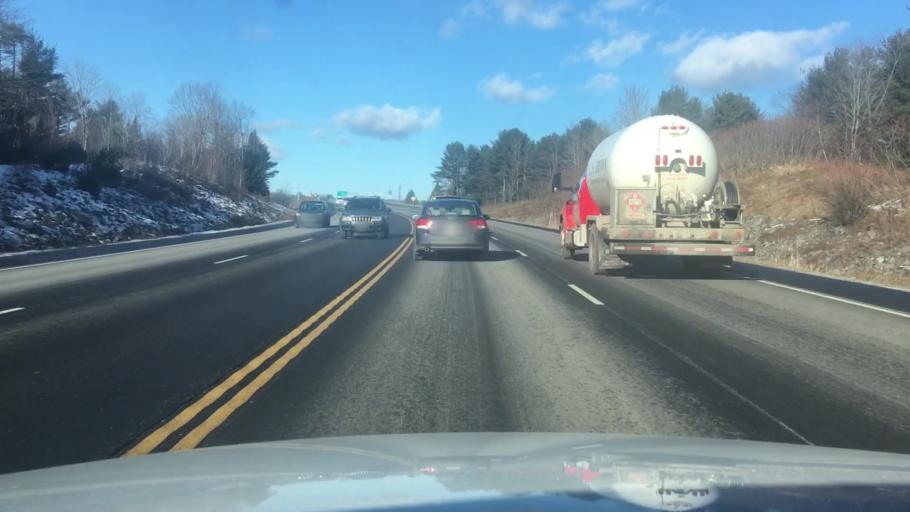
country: US
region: Maine
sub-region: Kennebec County
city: Augusta
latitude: 44.3491
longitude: -69.7738
